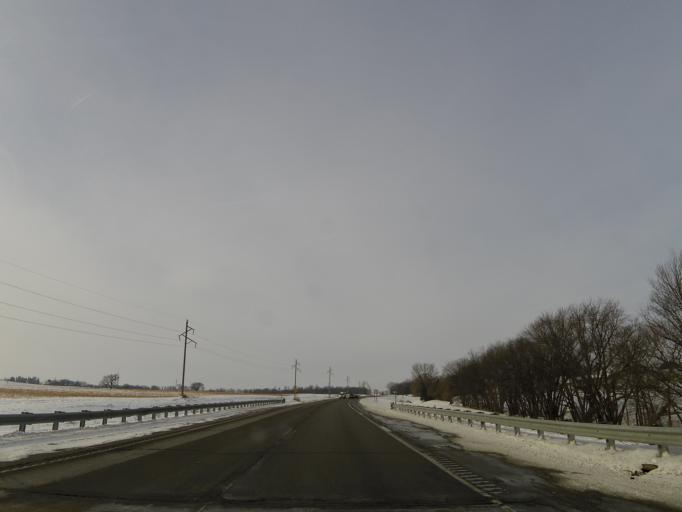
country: US
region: Minnesota
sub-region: Carver County
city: Mayer
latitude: 44.9055
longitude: -93.8857
